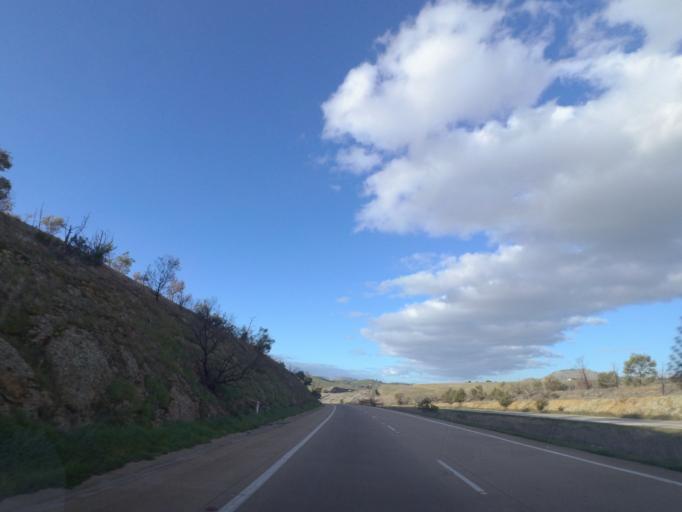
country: AU
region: New South Wales
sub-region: Gundagai
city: Gundagai
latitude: -34.8145
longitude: 148.4456
